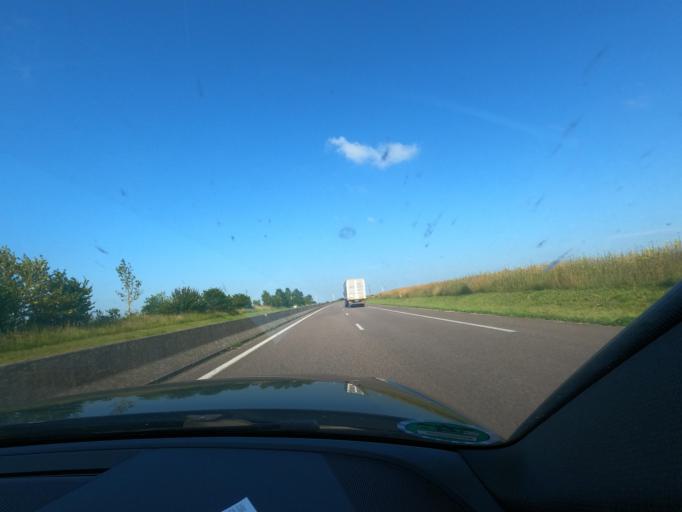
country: FR
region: Picardie
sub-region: Departement de la Somme
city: Hornoy-le-Bourg
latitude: 49.8125
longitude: 1.8693
